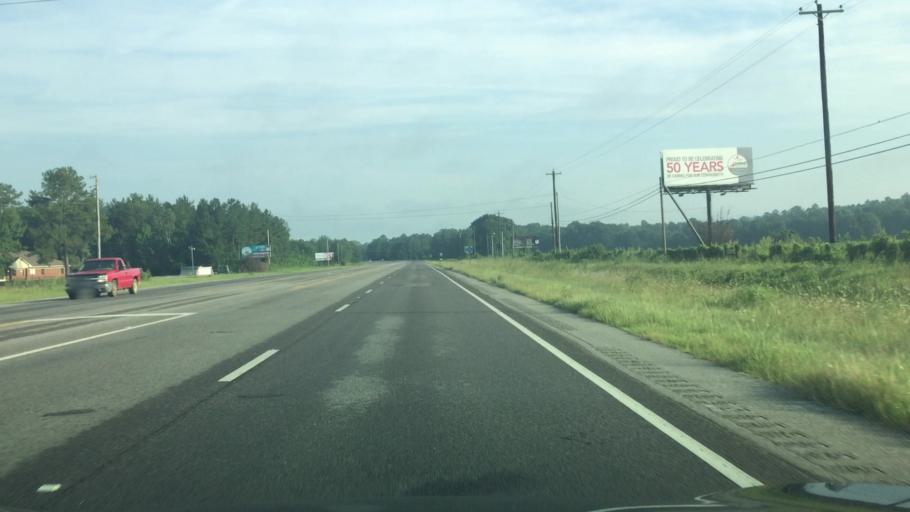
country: US
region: Alabama
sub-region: Covington County
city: Andalusia
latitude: 31.3405
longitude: -86.5228
